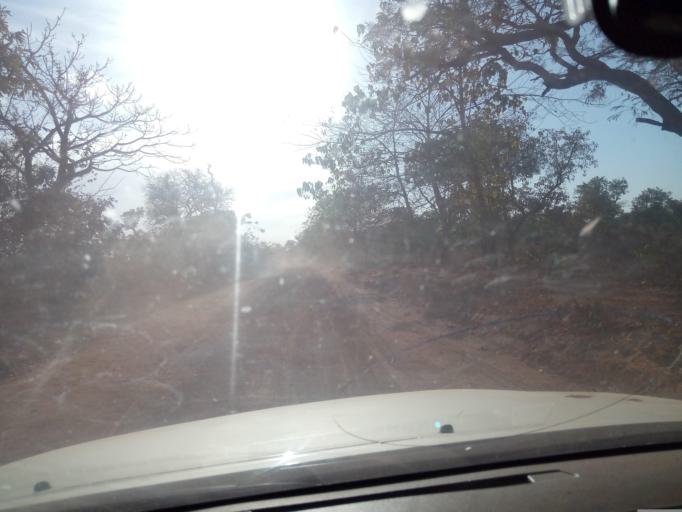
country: ML
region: Sikasso
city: Sikasso
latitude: 11.4372
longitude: -5.5549
